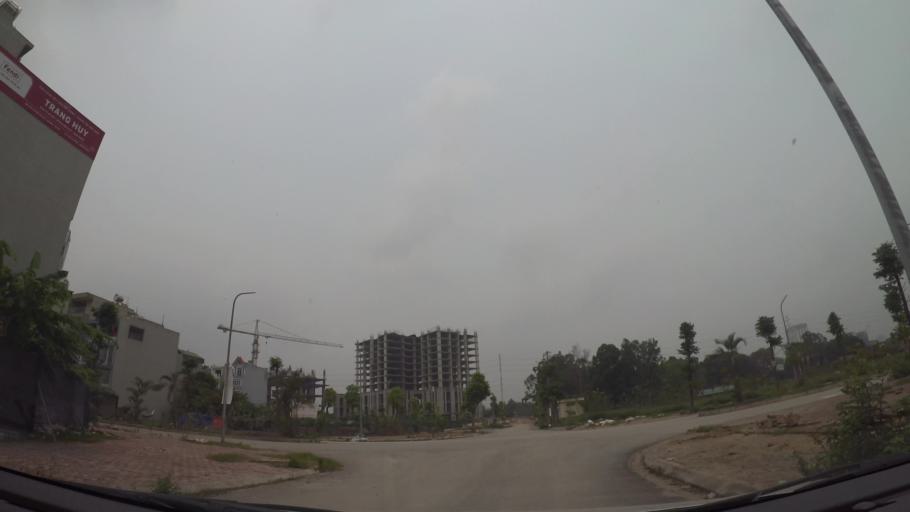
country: VN
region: Ha Noi
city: Ha Dong
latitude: 20.9771
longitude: 105.7671
